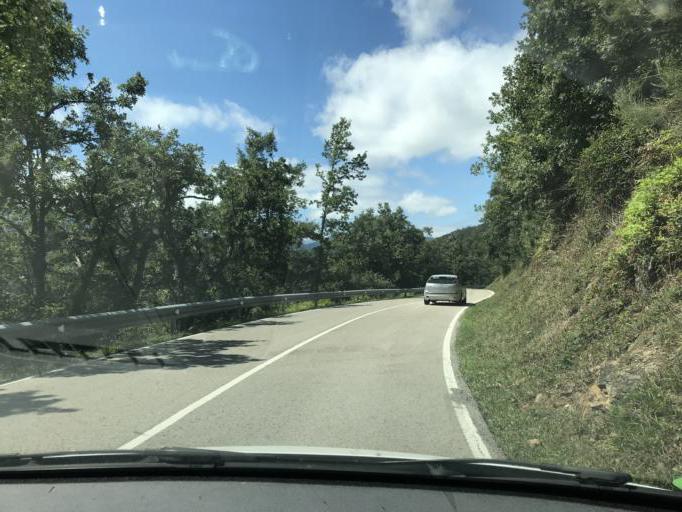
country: ES
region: Cantabria
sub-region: Provincia de Cantabria
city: Cabezon de Liebana
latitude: 43.0754
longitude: -4.4809
